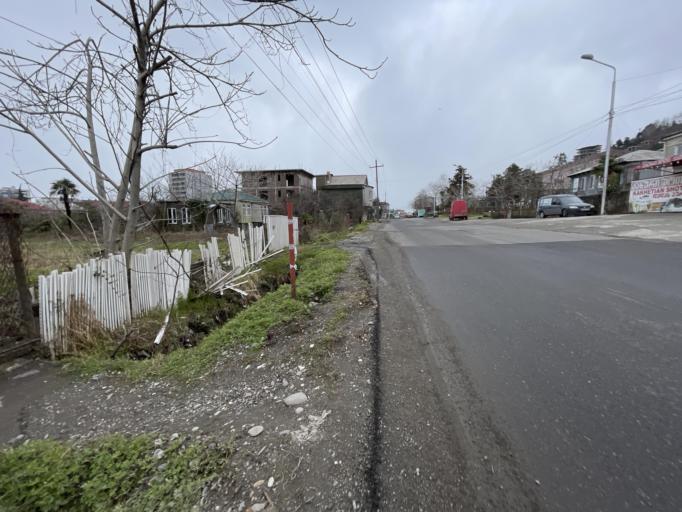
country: GE
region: Ajaria
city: Batumi
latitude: 41.6344
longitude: 41.6448
